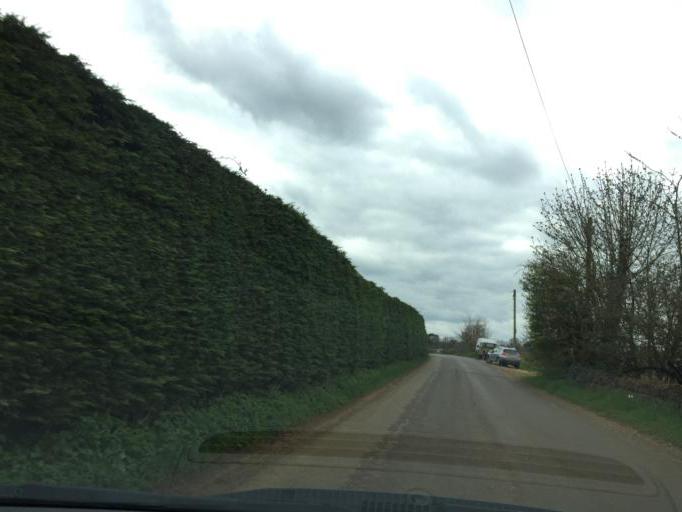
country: GB
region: England
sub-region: Oxfordshire
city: Hanwell
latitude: 52.1091
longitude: -1.4470
